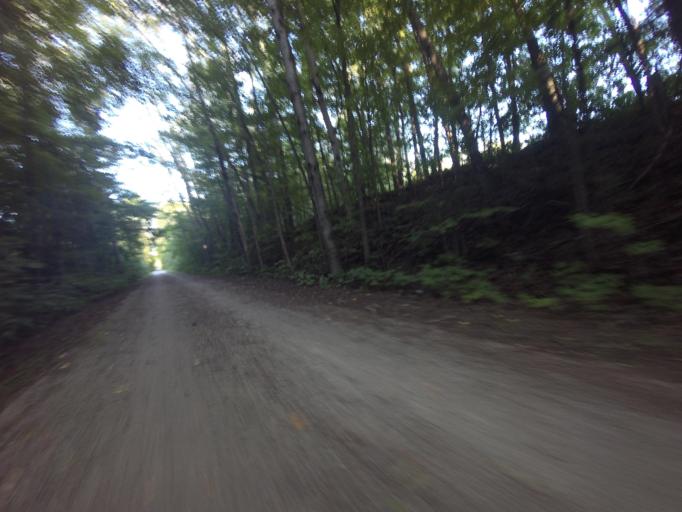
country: CA
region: Ontario
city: Brampton
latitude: 43.8325
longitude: -79.9004
